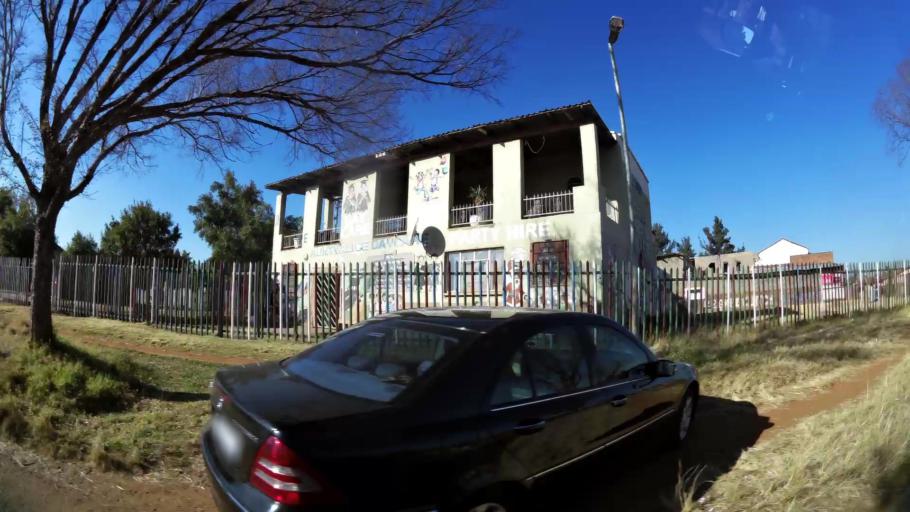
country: ZA
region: Gauteng
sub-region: City of Johannesburg Metropolitan Municipality
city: Roodepoort
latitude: -26.1544
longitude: 27.8513
